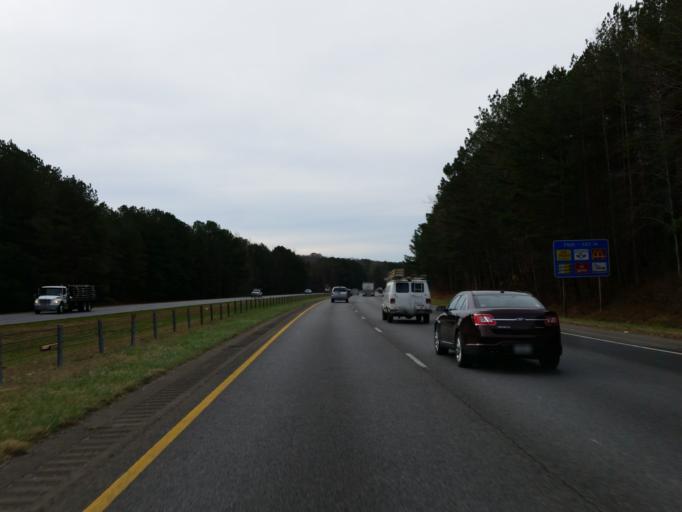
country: US
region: Georgia
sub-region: Cherokee County
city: Canton
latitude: 34.2066
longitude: -84.4936
